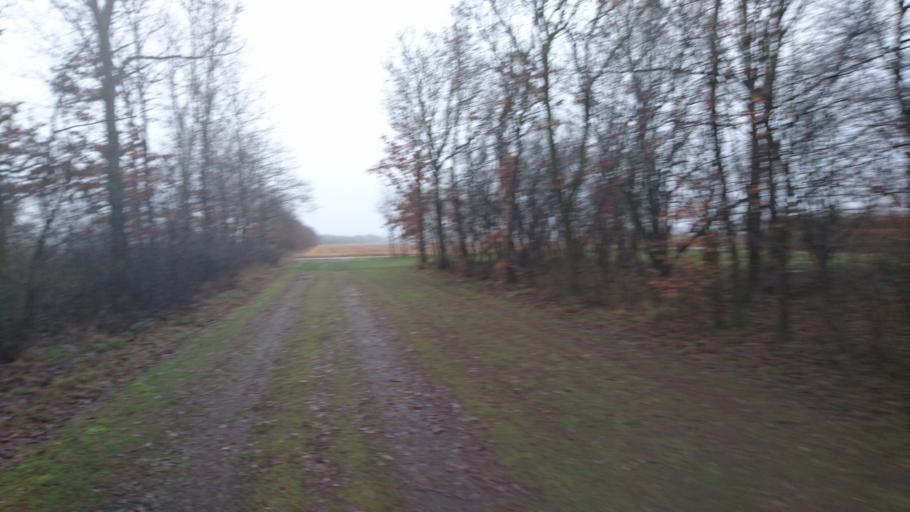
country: DK
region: Central Jutland
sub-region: Herning Kommune
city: Sunds
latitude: 56.1930
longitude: 9.0280
